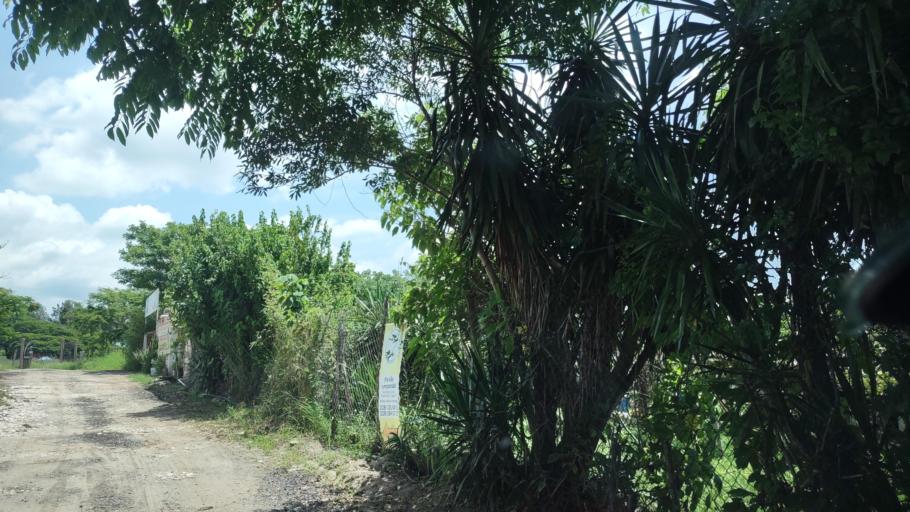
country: MX
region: Veracruz
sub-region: Emiliano Zapata
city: Dos Rios
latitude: 19.4664
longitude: -96.7919
